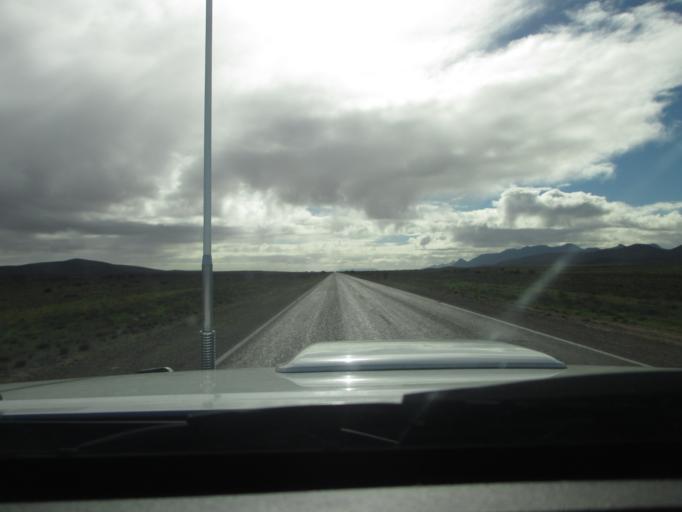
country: AU
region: South Australia
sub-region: Flinders Ranges
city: Quorn
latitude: -31.6552
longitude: 138.3777
